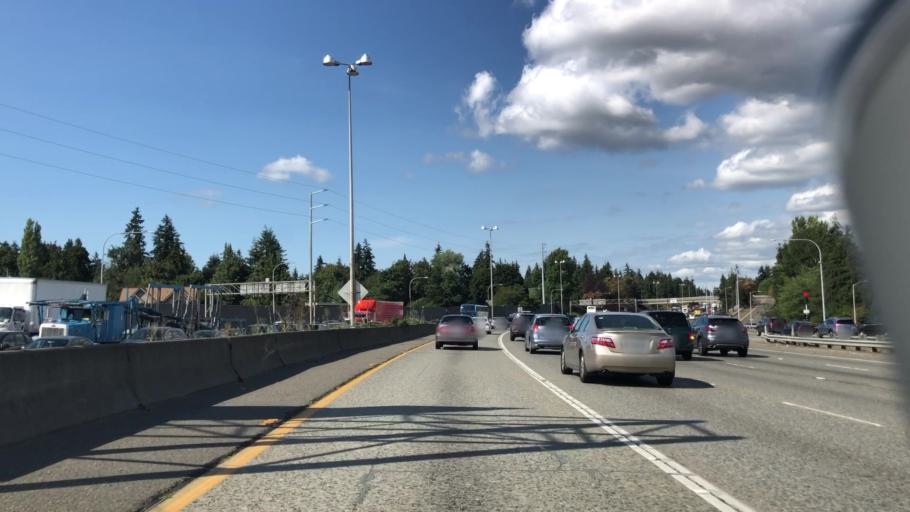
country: US
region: Washington
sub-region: King County
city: Shoreline
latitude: 47.7098
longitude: -122.3316
